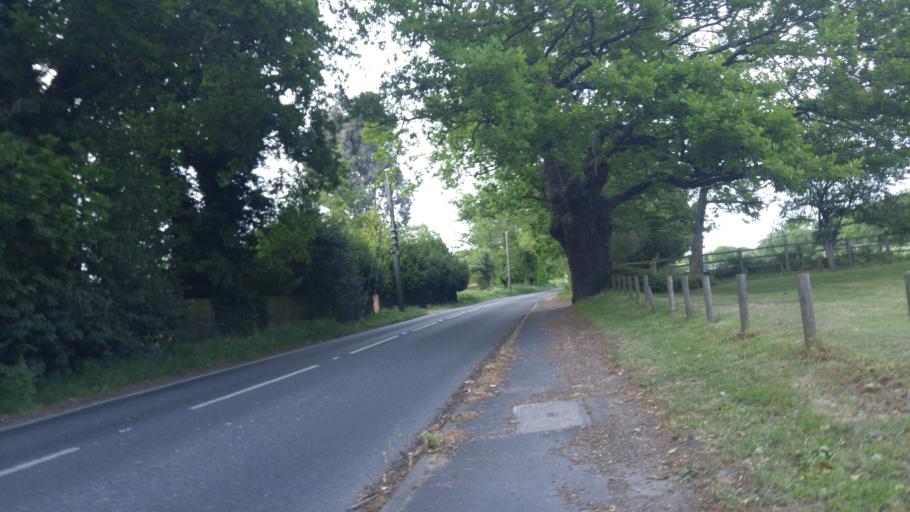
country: GB
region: England
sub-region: Essex
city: Layer de la Haye
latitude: 51.8602
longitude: 0.8679
